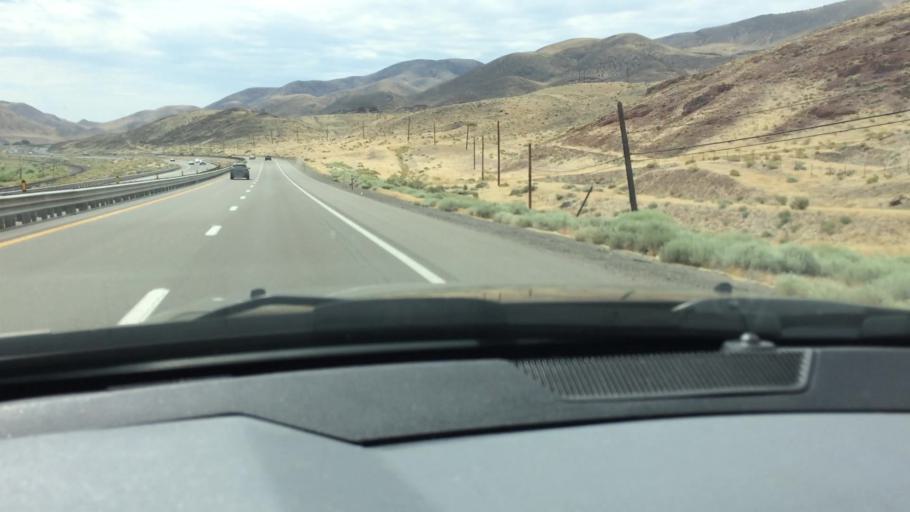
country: US
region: Nevada
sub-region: Lyon County
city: Fernley
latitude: 39.5913
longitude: -119.4090
